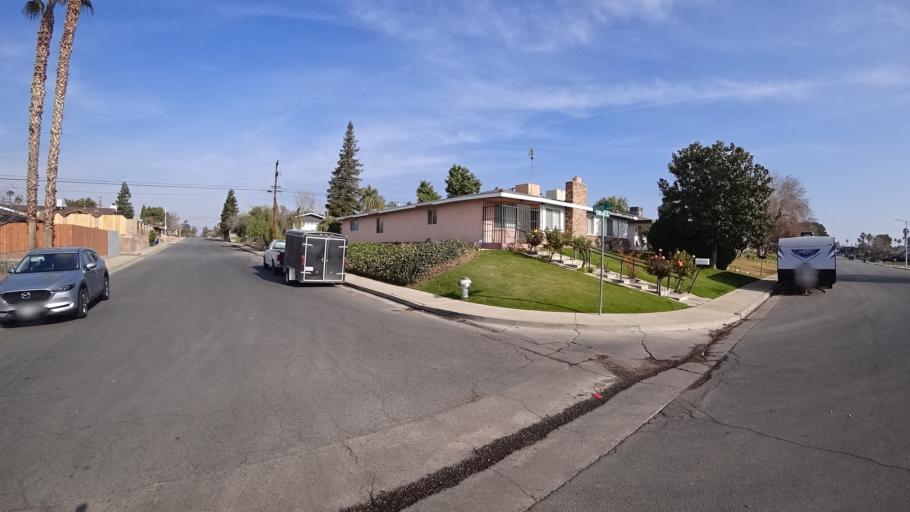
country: US
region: California
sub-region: Kern County
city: Oildale
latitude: 35.4060
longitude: -118.9546
